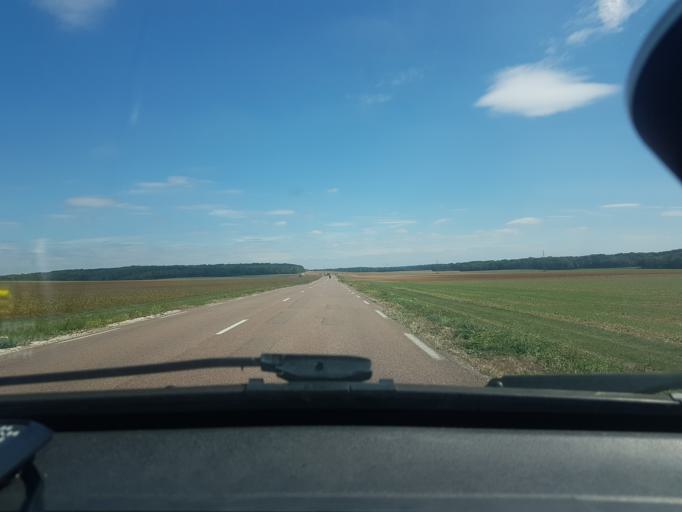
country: FR
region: Bourgogne
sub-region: Departement de la Cote-d'Or
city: Pontailler-sur-Saone
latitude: 47.3987
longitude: 5.4284
